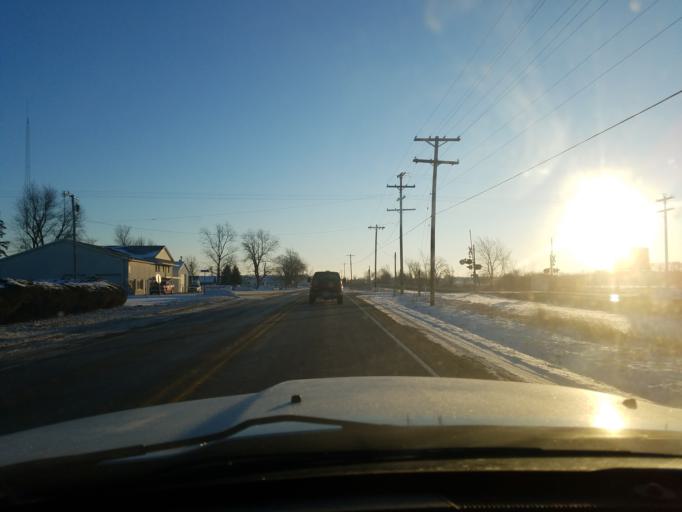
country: US
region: Indiana
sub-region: Marshall County
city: Bremen
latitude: 41.4470
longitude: -86.0793
